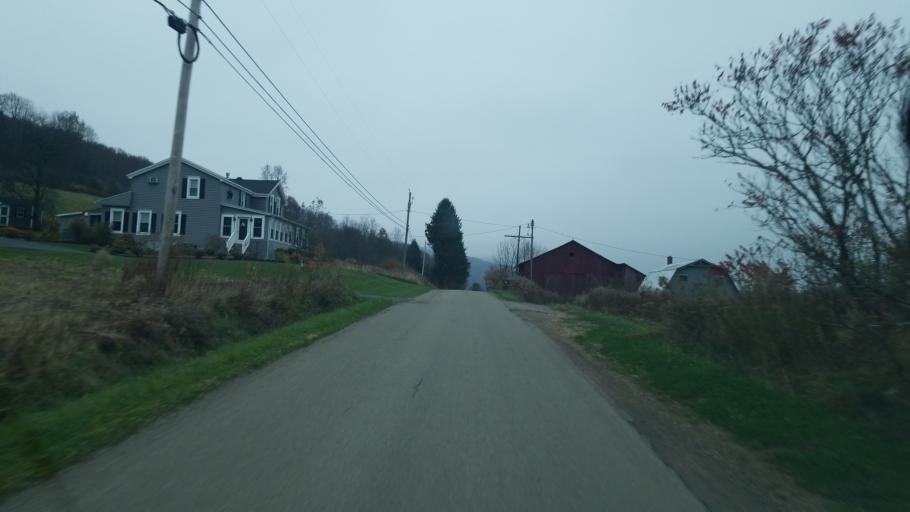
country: US
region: Pennsylvania
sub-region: McKean County
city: Smethport
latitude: 41.7892
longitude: -78.4265
